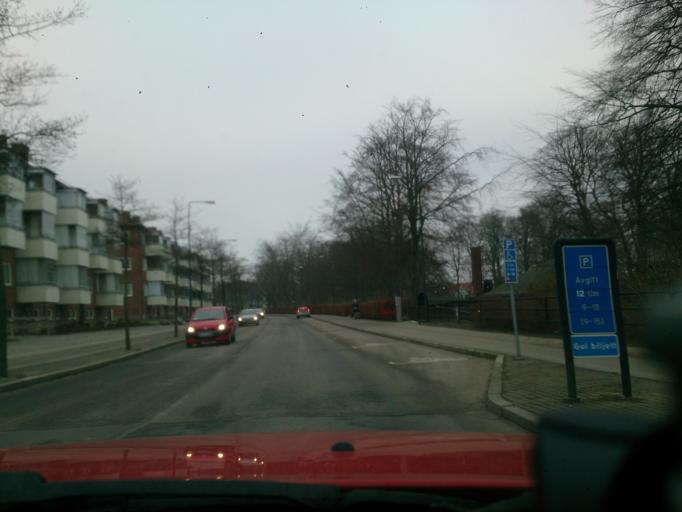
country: SE
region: Skane
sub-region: Ystads Kommun
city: Ystad
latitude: 55.4298
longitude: 13.8124
